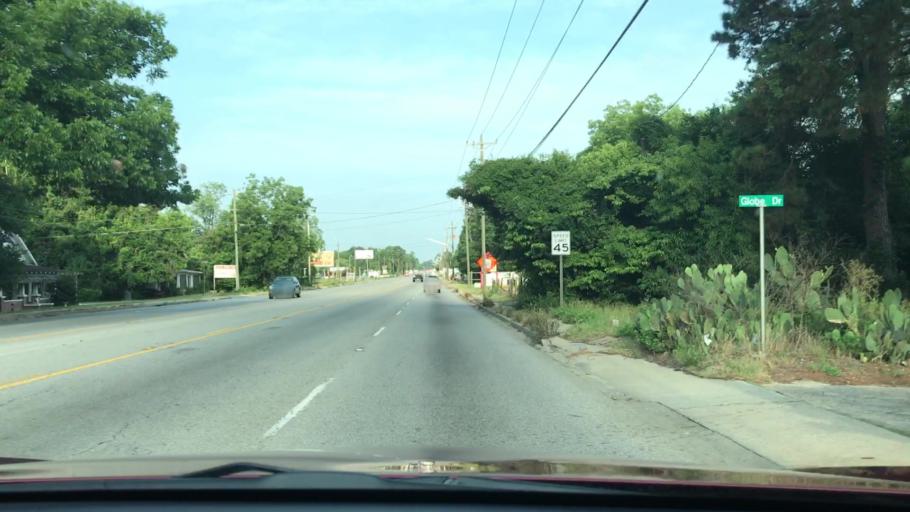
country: US
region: South Carolina
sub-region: Orangeburg County
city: Edisto
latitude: 33.4817
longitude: -80.8879
